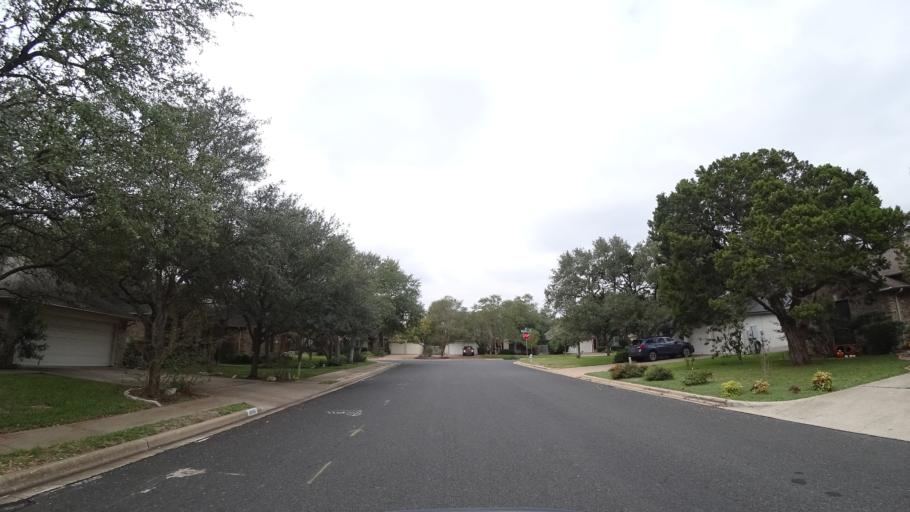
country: US
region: Texas
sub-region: Travis County
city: Shady Hollow
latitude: 30.2152
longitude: -97.8796
